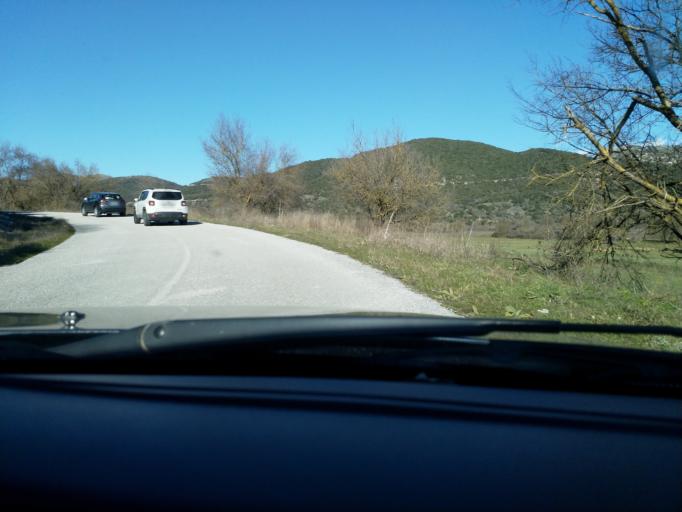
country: GR
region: Epirus
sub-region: Nomos Ioanninon
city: Kalpaki
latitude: 39.8877
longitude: 20.6731
